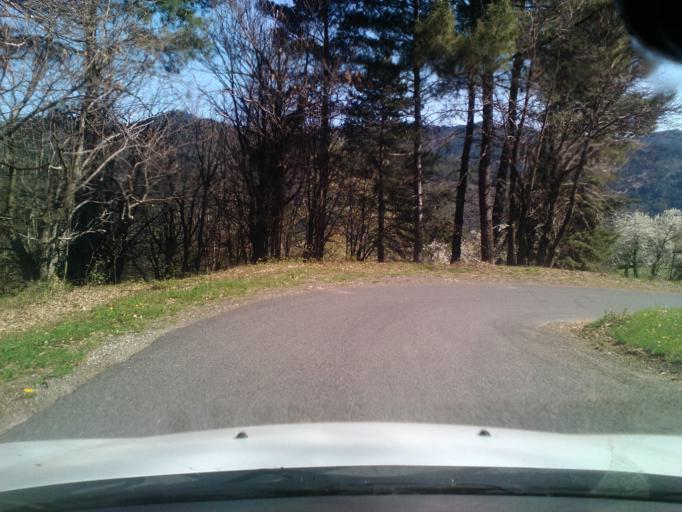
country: FR
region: Languedoc-Roussillon
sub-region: Departement du Gard
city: Saint-Jean-du-Gard
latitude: 44.1582
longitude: 3.7672
